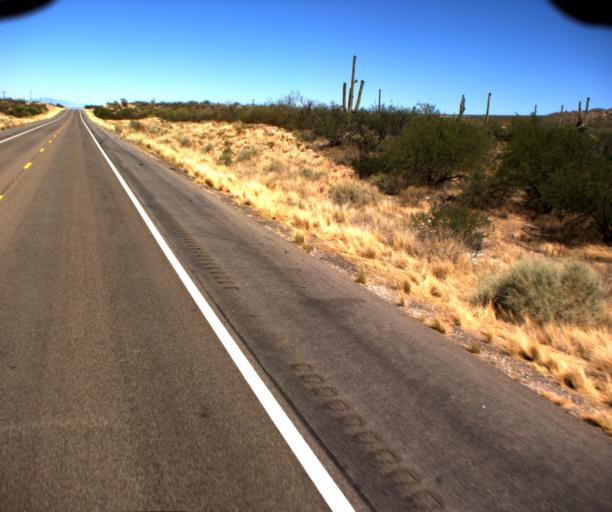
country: US
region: Arizona
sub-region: Pima County
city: Three Points
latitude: 32.0368
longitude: -111.5284
